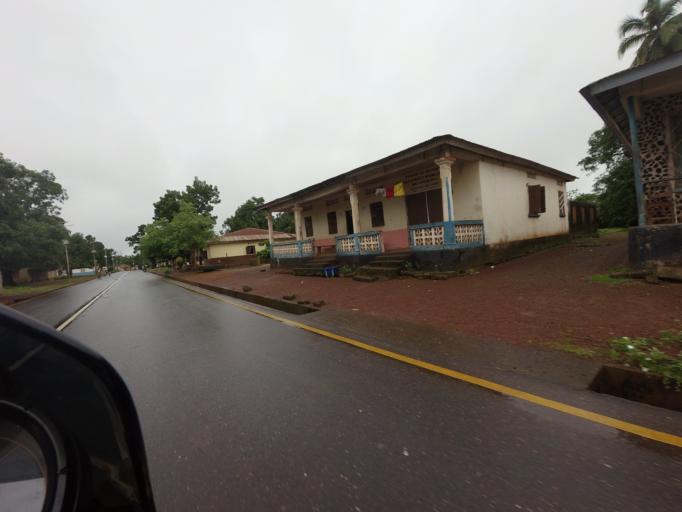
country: SL
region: Northern Province
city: Kambia
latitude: 9.1260
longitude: -12.9141
